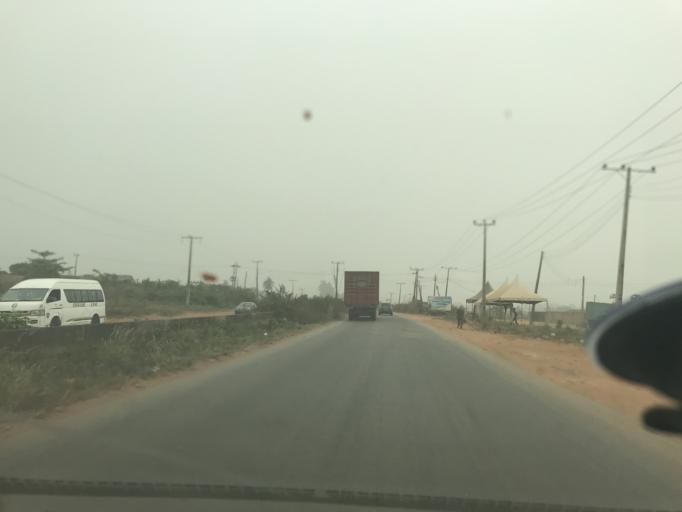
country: NG
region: Ogun
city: Shagamu
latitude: 6.8678
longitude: 3.6035
